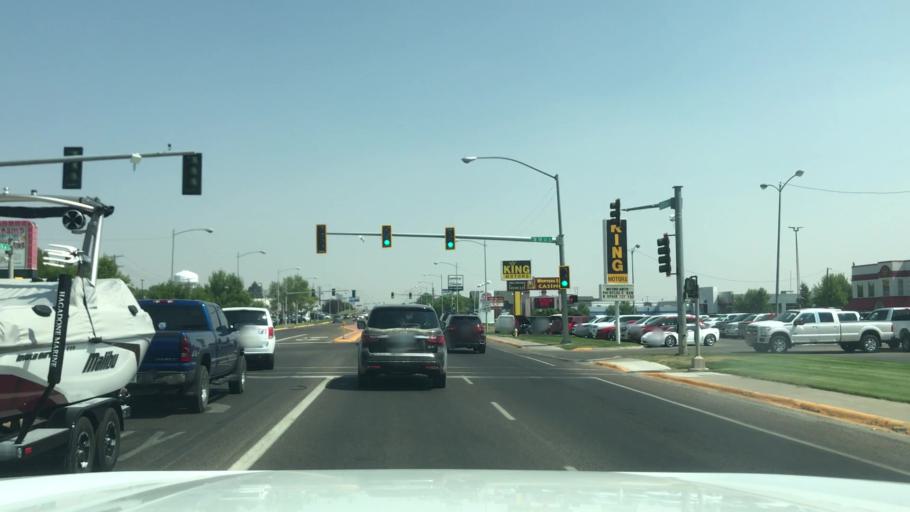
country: US
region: Montana
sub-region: Cascade County
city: Great Falls
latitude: 47.4940
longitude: -111.2422
